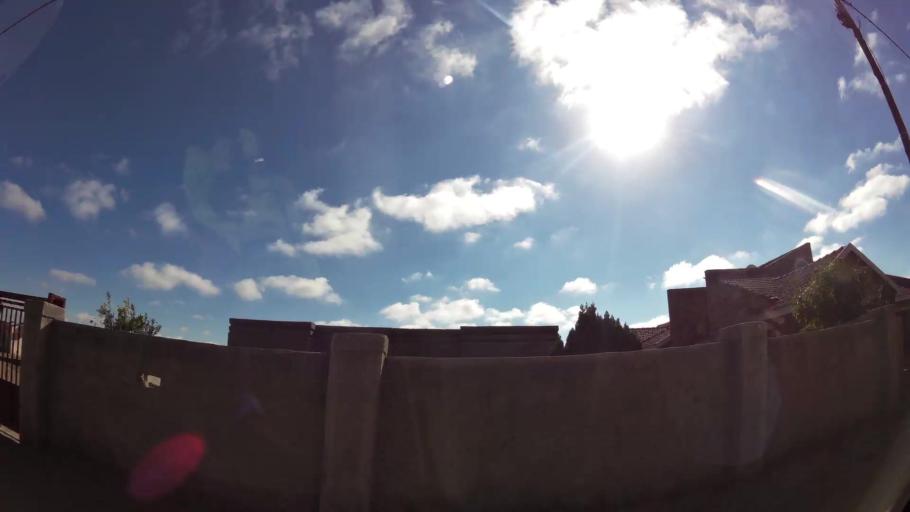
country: ZA
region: Limpopo
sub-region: Capricorn District Municipality
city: Polokwane
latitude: -23.8444
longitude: 29.4033
